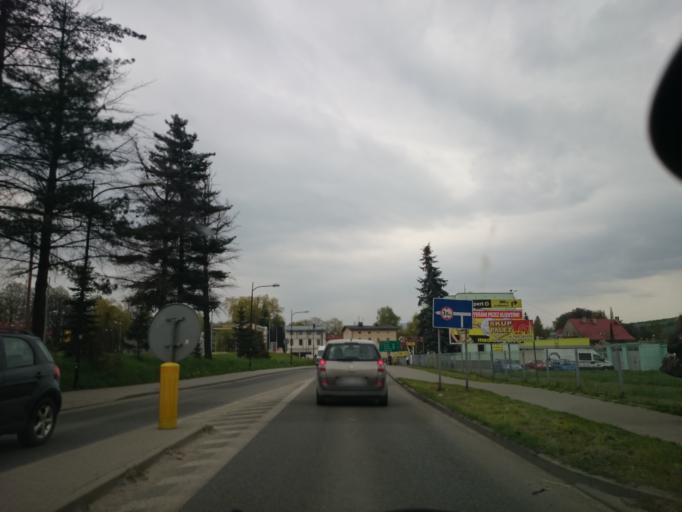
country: PL
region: Opole Voivodeship
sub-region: Powiat nyski
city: Glucholazy
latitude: 50.3182
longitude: 17.3882
